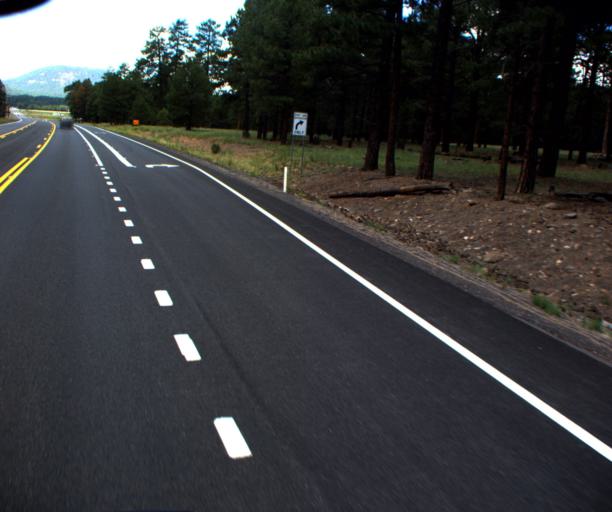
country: US
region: Arizona
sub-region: Coconino County
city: Flagstaff
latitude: 35.2685
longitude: -111.7151
